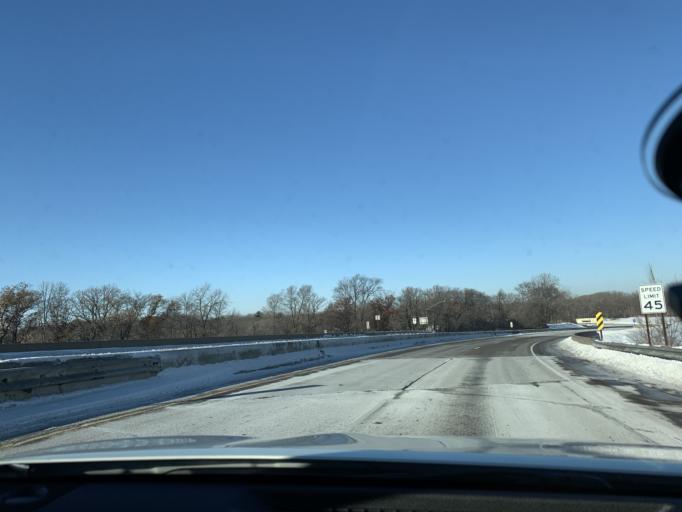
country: US
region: Minnesota
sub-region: Anoka County
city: Coon Rapids
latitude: 45.1471
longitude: -93.2930
